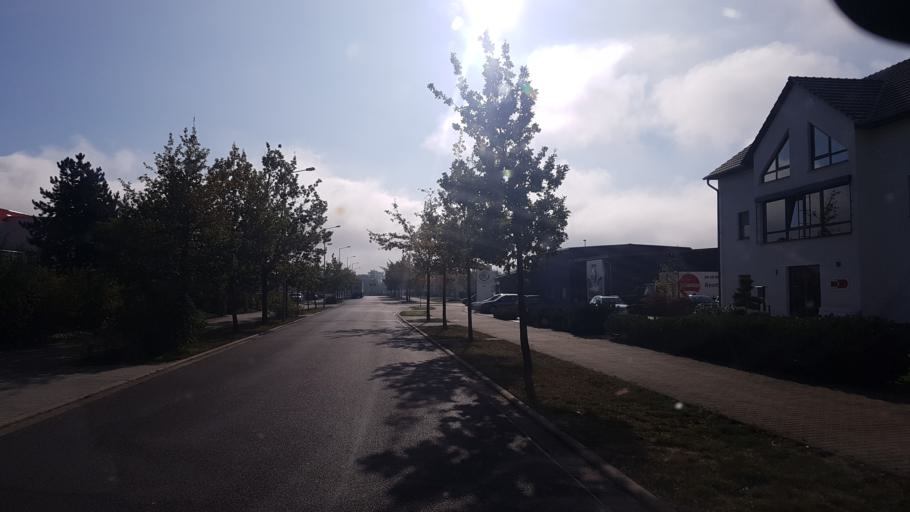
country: DE
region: Brandenburg
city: Elsterwerda
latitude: 51.4630
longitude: 13.5382
